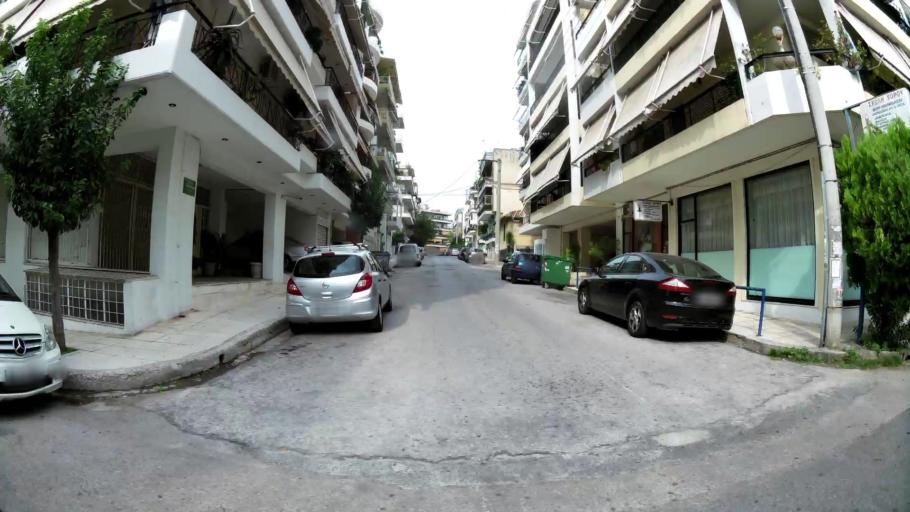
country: GR
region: Attica
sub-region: Nomarchia Athinas
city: Nea Filadelfeia
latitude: 38.0315
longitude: 23.7461
